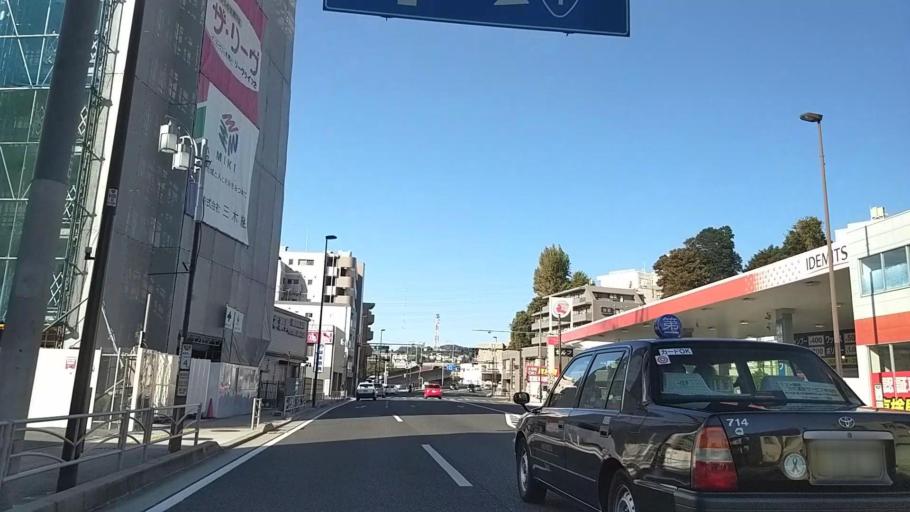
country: JP
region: Kanagawa
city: Yokohama
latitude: 35.4654
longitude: 139.5862
